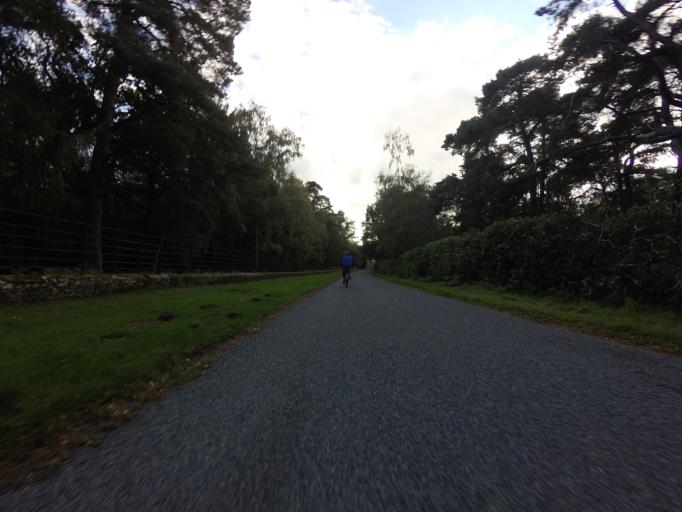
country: GB
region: England
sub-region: Norfolk
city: Dersingham
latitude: 52.8209
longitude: 0.4961
